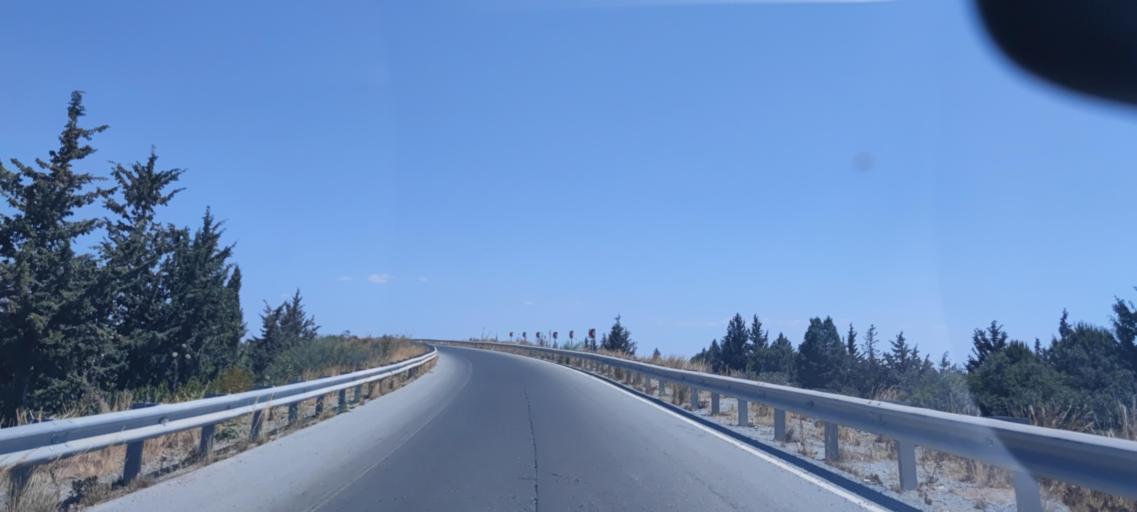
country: CY
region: Larnaka
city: Kolossi
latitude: 34.6885
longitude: 32.9407
